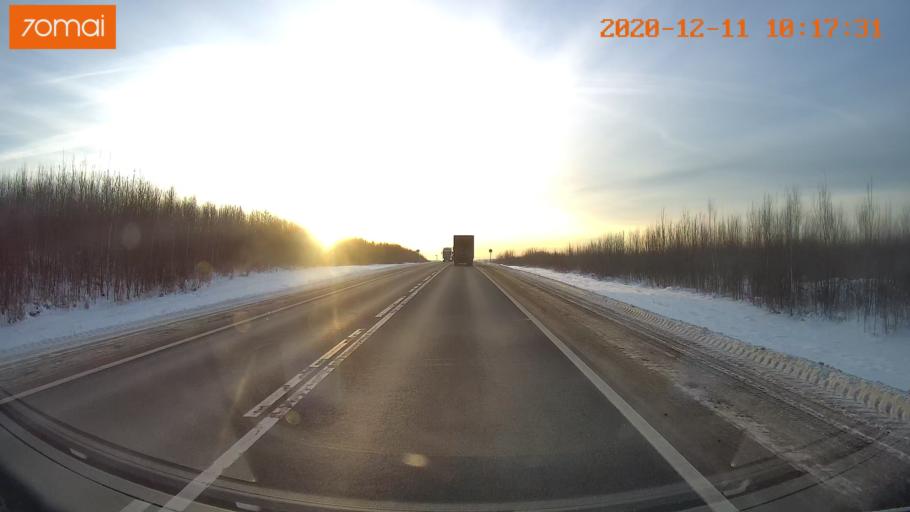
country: RU
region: Jaroslavl
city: Prechistoye
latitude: 58.6233
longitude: 40.3313
